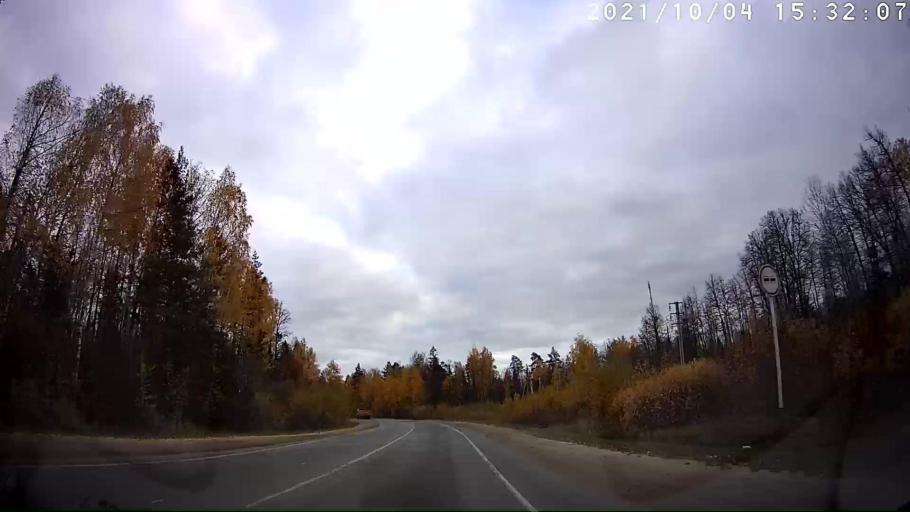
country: RU
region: Mariy-El
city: Yoshkar-Ola
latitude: 56.5722
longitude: 47.9708
